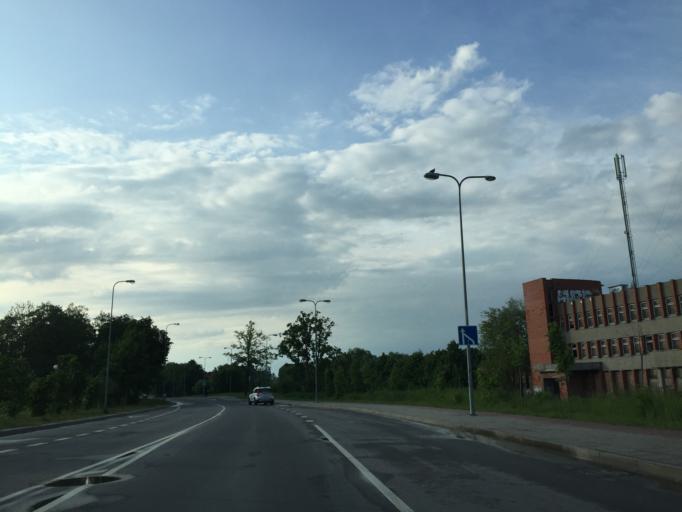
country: LT
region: Klaipedos apskritis
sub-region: Klaipeda
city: Klaipeda
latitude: 55.7532
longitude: 21.1330
